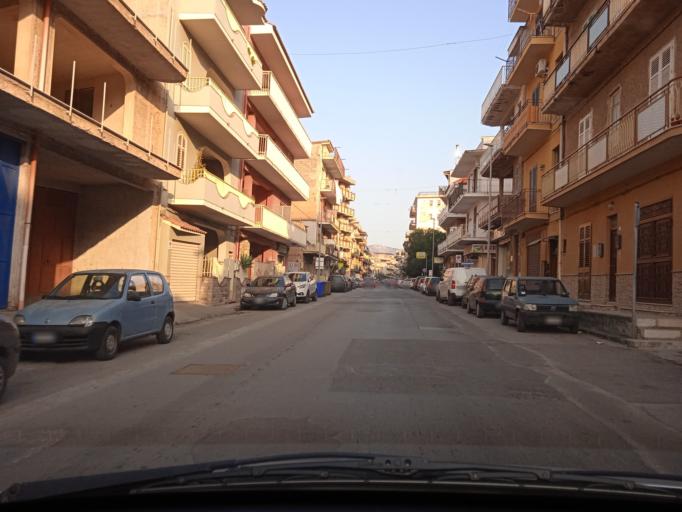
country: IT
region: Sicily
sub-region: Palermo
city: Villabate
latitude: 38.0755
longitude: 13.4460
